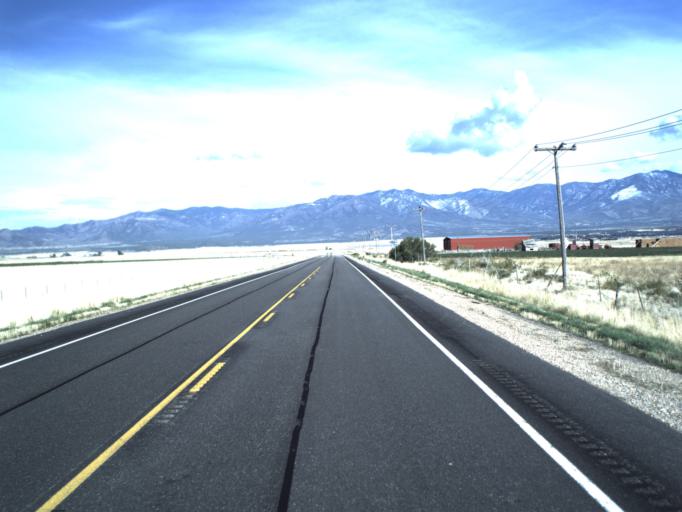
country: US
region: Utah
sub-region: Millard County
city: Fillmore
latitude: 39.1181
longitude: -112.3479
